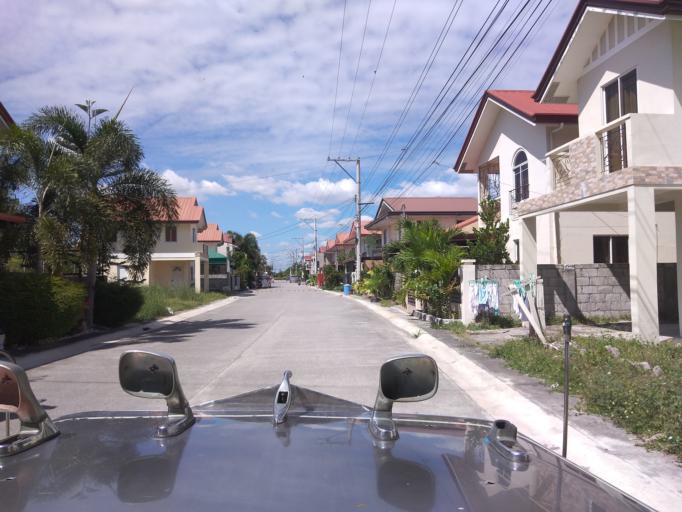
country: PH
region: Central Luzon
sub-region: Province of Pampanga
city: Magliman
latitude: 15.0391
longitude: 120.6556
